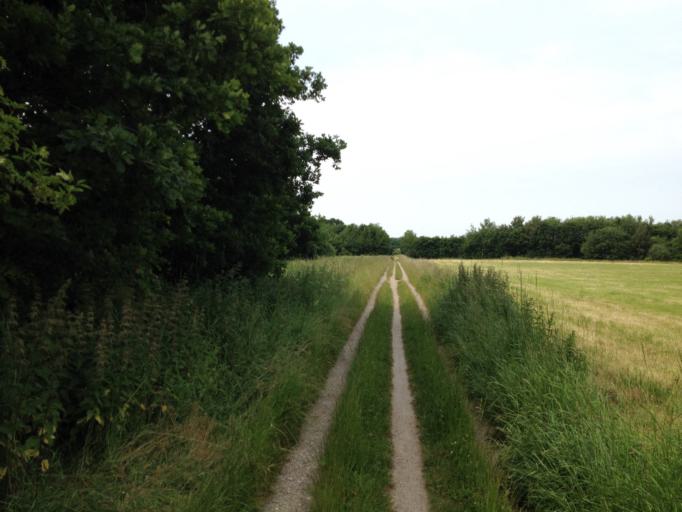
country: DK
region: Capital Region
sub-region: Fredensborg Kommune
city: Niva
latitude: 55.9469
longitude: 12.5091
